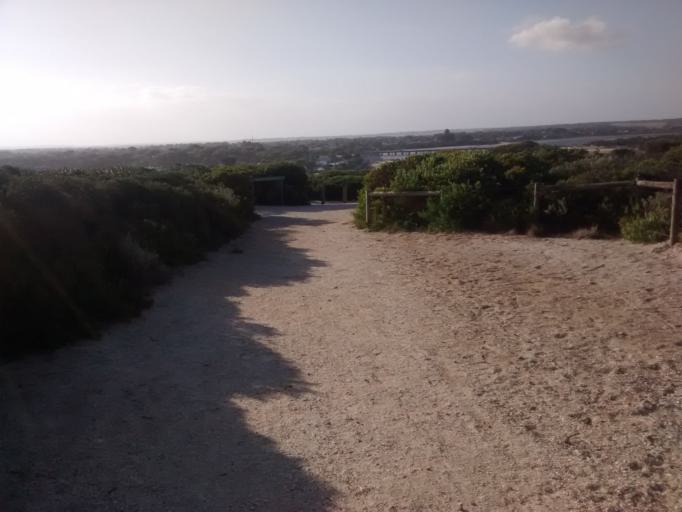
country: AU
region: Victoria
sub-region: Greater Geelong
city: Leopold
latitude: -38.2898
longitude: 144.4985
